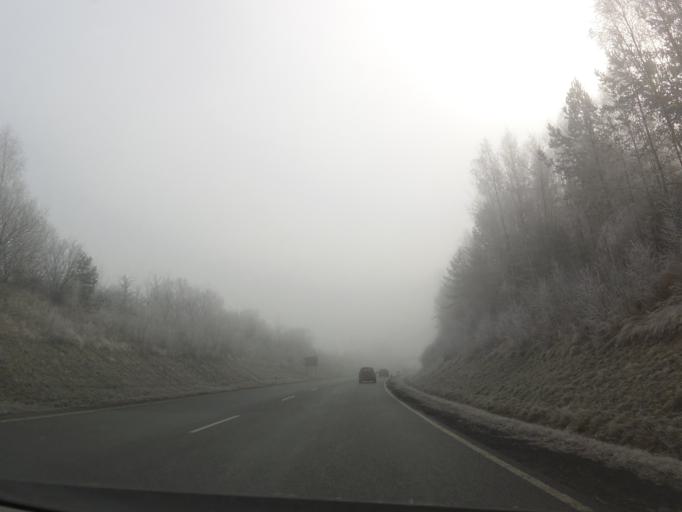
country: DE
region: Bavaria
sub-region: Upper Franconia
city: Schirnding
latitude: 50.0870
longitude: 12.2281
